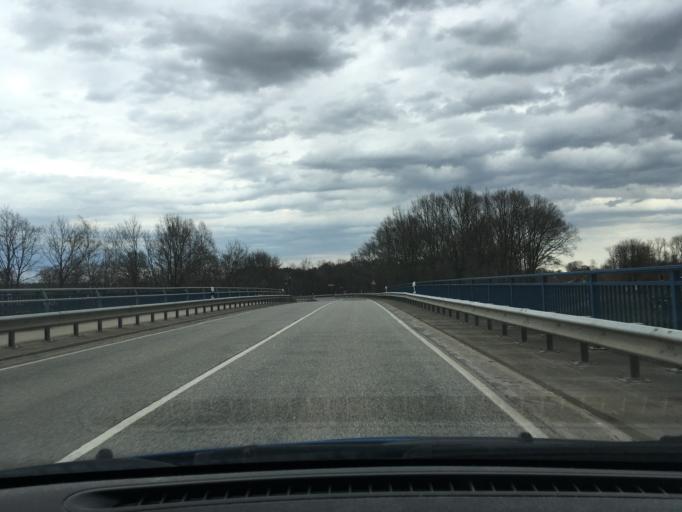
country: DE
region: Lower Saxony
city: Winsen
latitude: 53.3760
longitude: 10.2432
